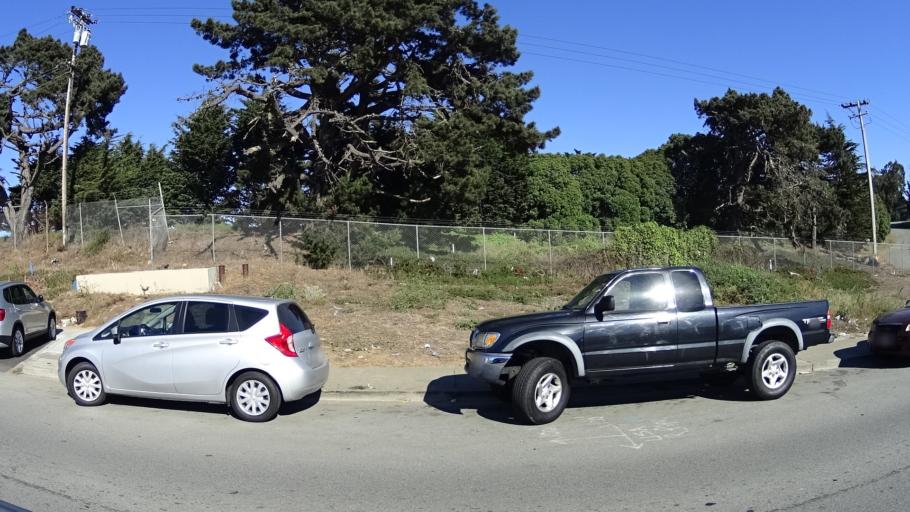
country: US
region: California
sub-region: San Mateo County
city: Broadmoor
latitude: 37.6956
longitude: -122.4801
